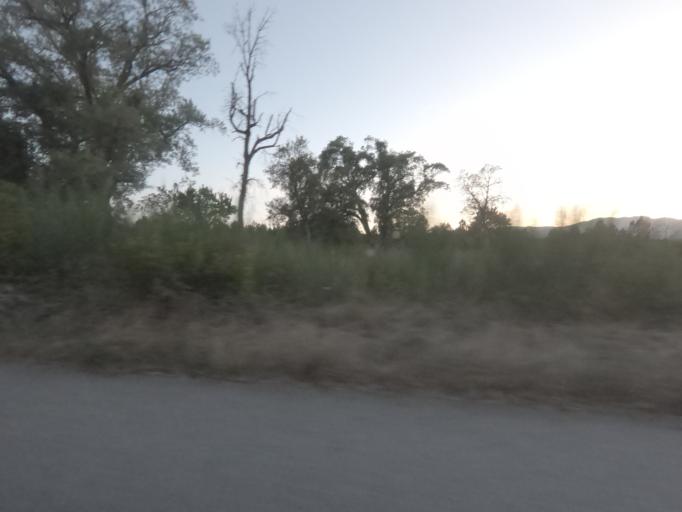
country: PT
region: Vila Real
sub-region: Peso da Regua
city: Peso da Regua
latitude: 41.1883
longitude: -7.7103
